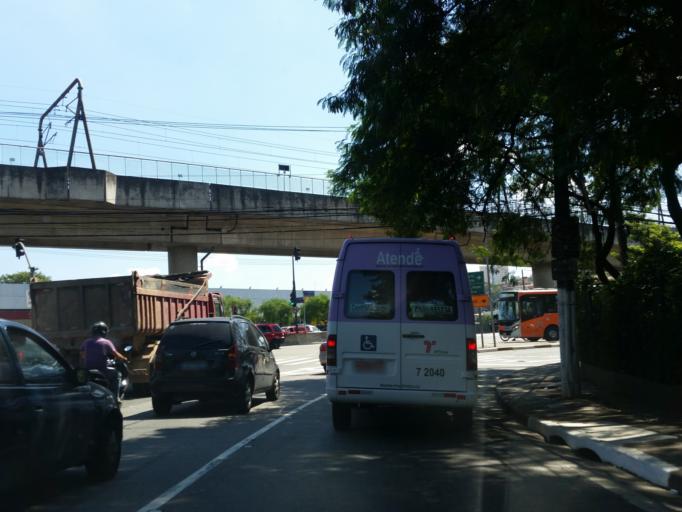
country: BR
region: Sao Paulo
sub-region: Taboao Da Serra
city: Taboao da Serra
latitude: -23.6407
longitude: -46.7365
